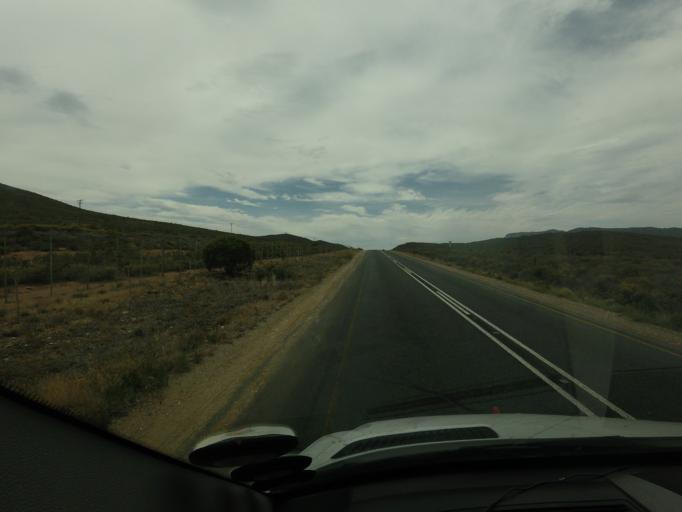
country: ZA
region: Western Cape
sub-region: Overberg District Municipality
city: Swellendam
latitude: -33.8905
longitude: 20.7321
